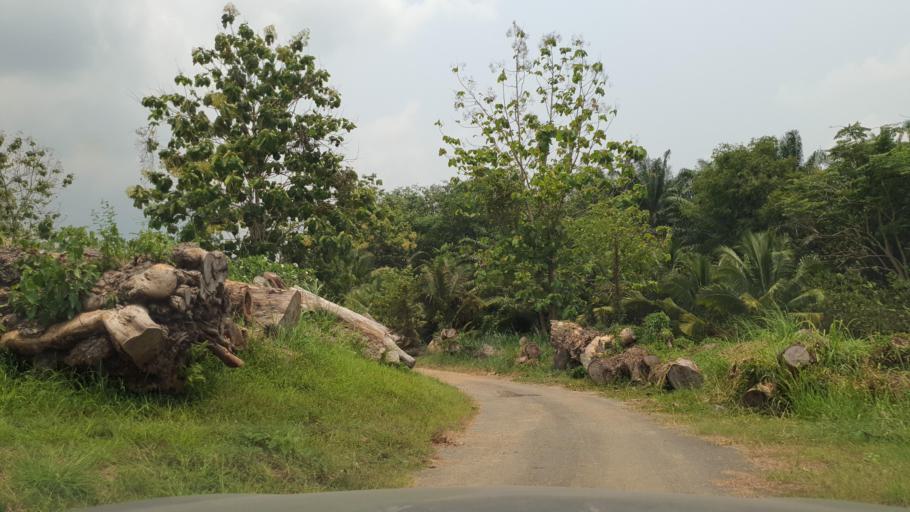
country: TH
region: Rayong
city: Ban Chang
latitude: 12.7667
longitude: 100.9895
